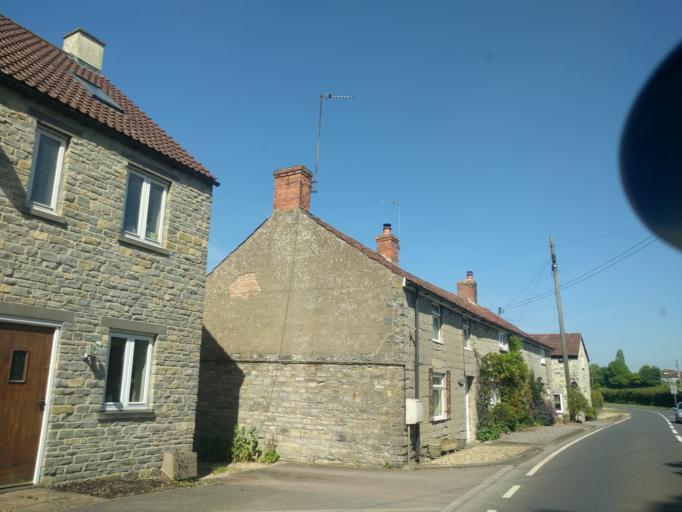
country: GB
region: England
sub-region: Somerset
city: Martock
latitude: 51.0312
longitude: -2.7623
